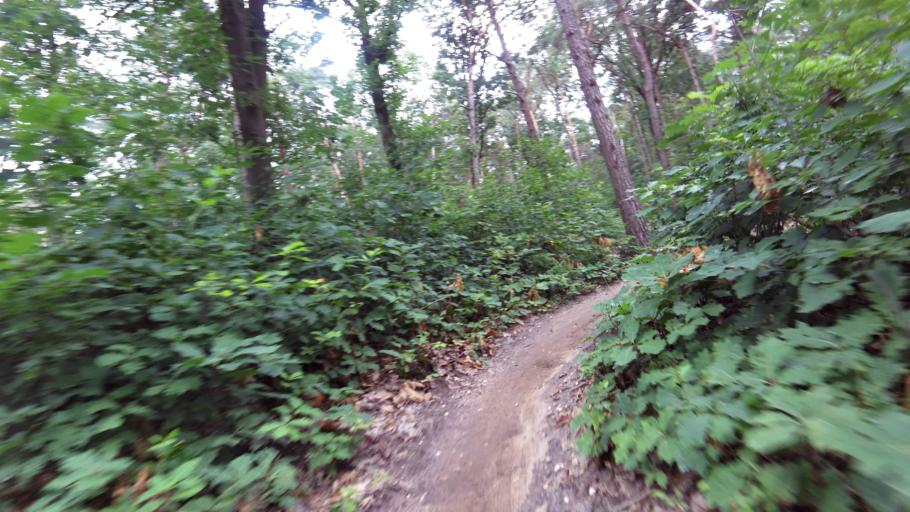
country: NL
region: Utrecht
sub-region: Gemeente Utrechtse Heuvelrug
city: Amerongen
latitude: 51.9958
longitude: 5.4977
